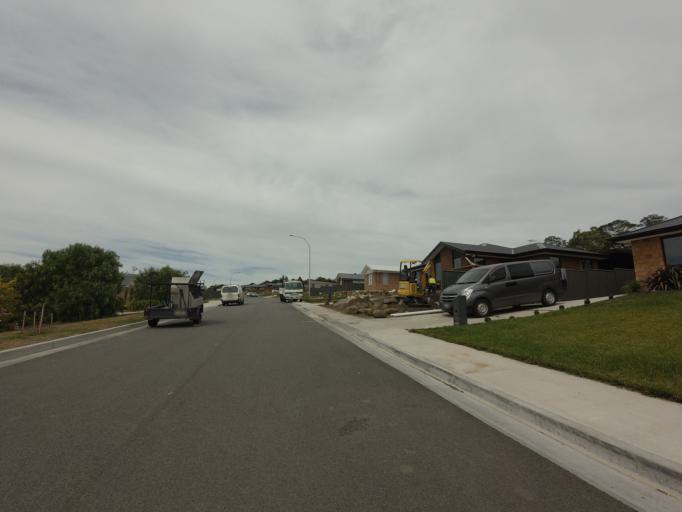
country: AU
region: Tasmania
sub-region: Sorell
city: Sorell
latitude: -42.7913
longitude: 147.5295
